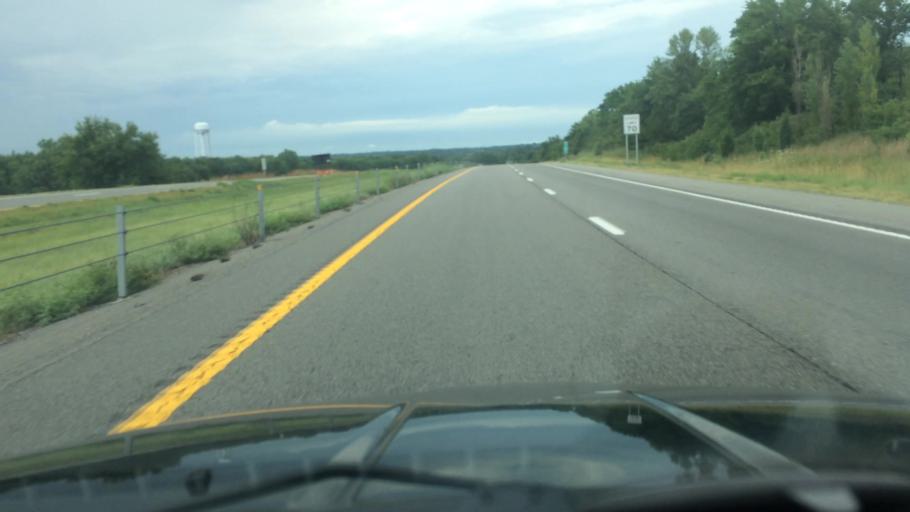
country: US
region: Missouri
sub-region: Cass County
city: Peculiar
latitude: 38.7473
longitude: -94.4772
